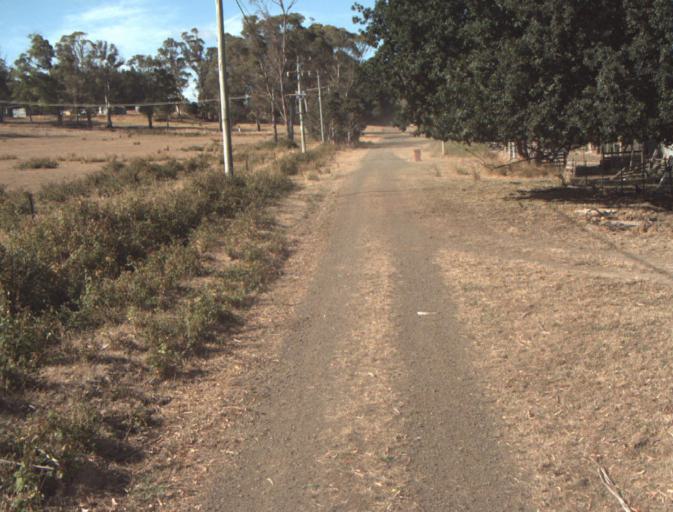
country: AU
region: Tasmania
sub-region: Dorset
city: Bridport
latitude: -41.1423
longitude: 147.2126
